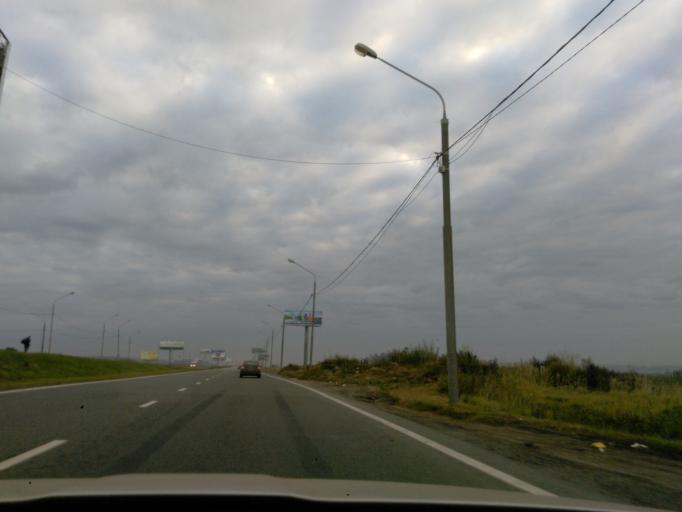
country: RU
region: Moskovskaya
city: Novopodrezkovo
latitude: 55.9558
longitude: 37.3481
